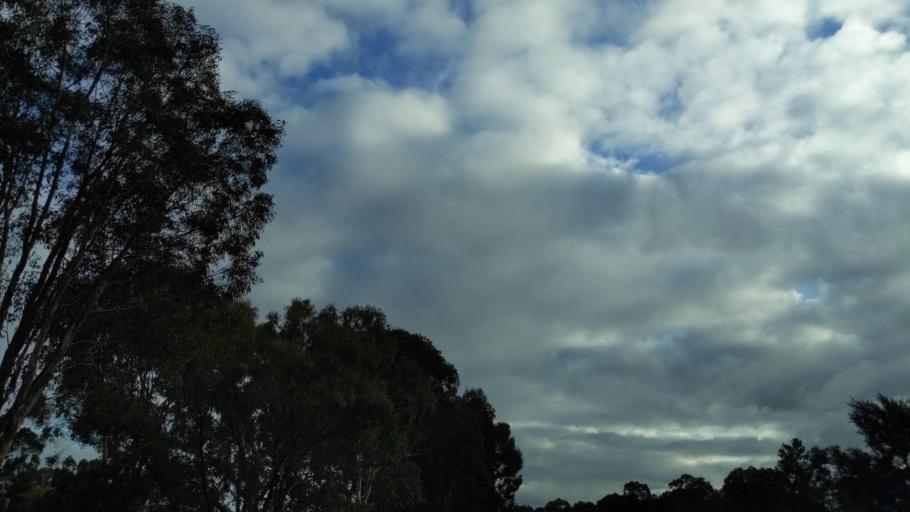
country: AU
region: New South Wales
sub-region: Wagga Wagga
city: Wagga Wagga
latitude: -35.0695
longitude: 147.3840
